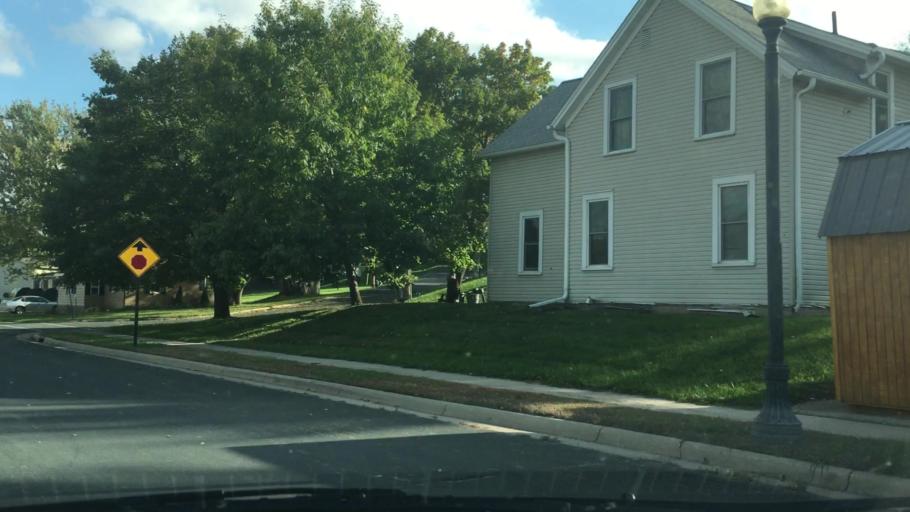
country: US
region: Minnesota
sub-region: Fillmore County
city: Preston
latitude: 43.6752
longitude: -92.0849
